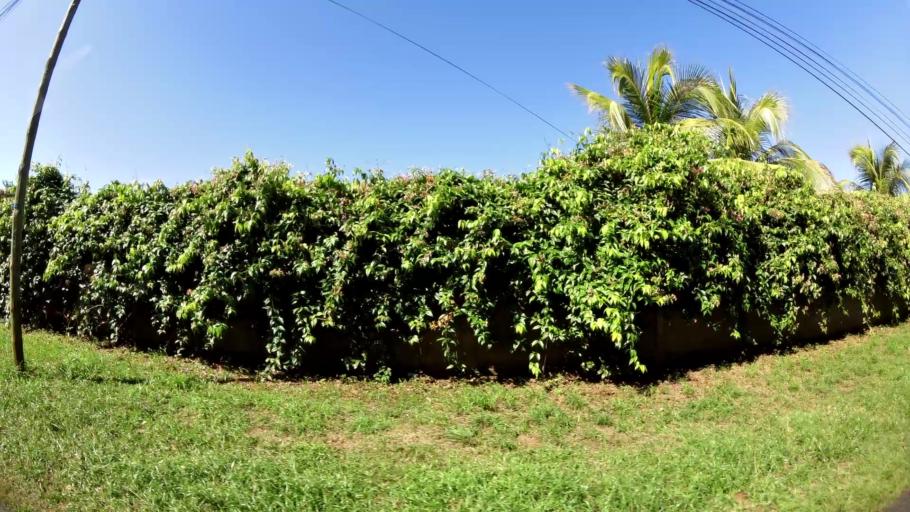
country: GF
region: Guyane
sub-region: Guyane
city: Remire-Montjoly
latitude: 4.9215
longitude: -52.2778
